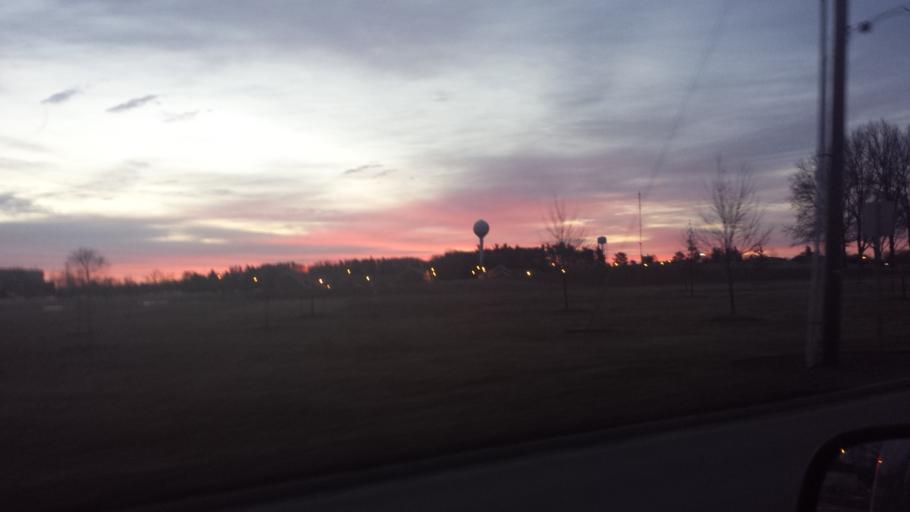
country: US
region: Ohio
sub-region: Wayne County
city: Wooster
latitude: 40.7784
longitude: -81.9309
